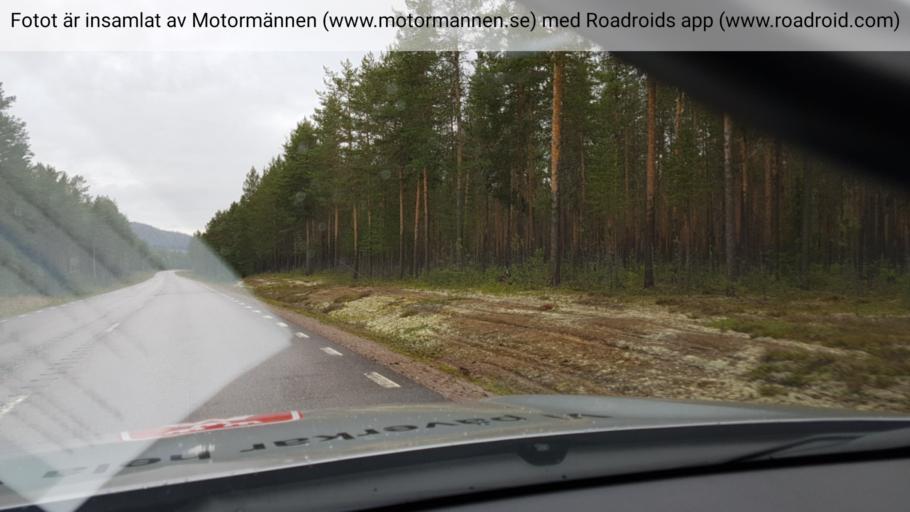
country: SE
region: Norrbotten
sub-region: Alvsbyns Kommun
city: AElvsbyn
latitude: 66.1373
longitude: 20.8929
